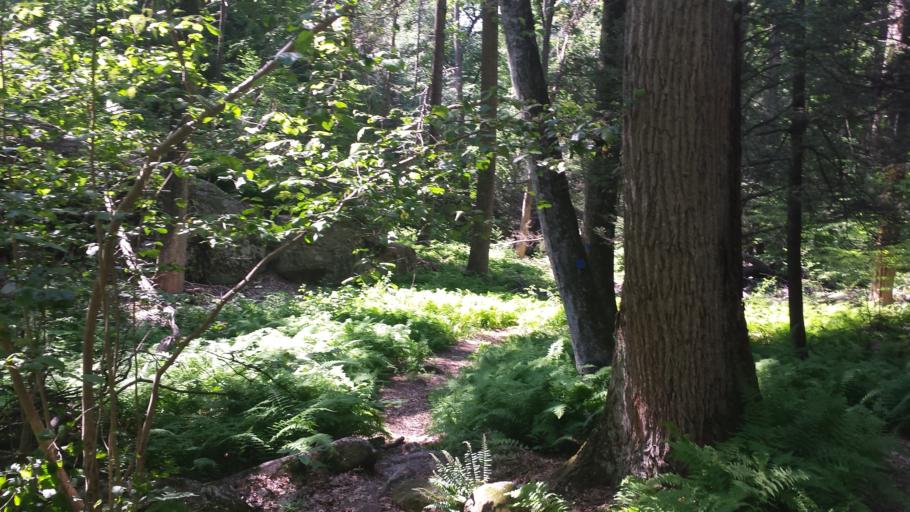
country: US
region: New York
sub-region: Westchester County
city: Pound Ridge
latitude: 41.2428
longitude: -73.5736
